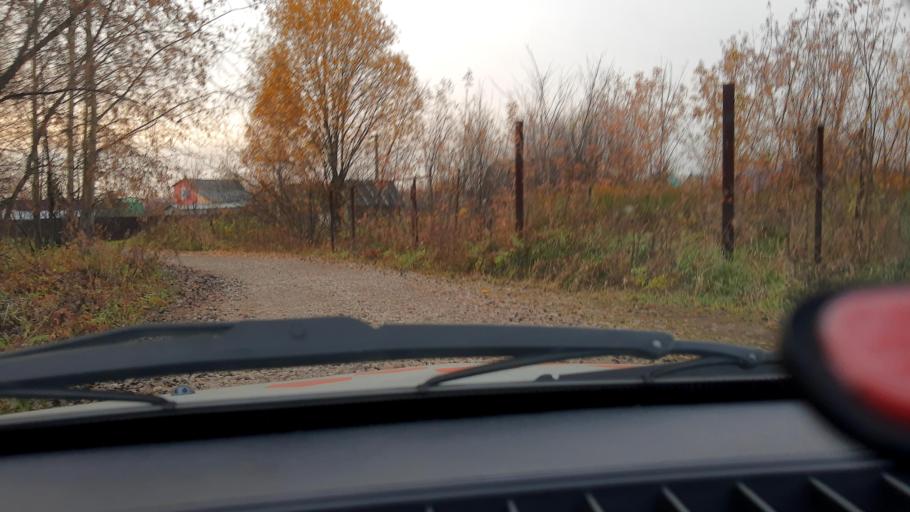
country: RU
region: Bashkortostan
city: Iglino
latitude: 54.7982
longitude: 56.3437
